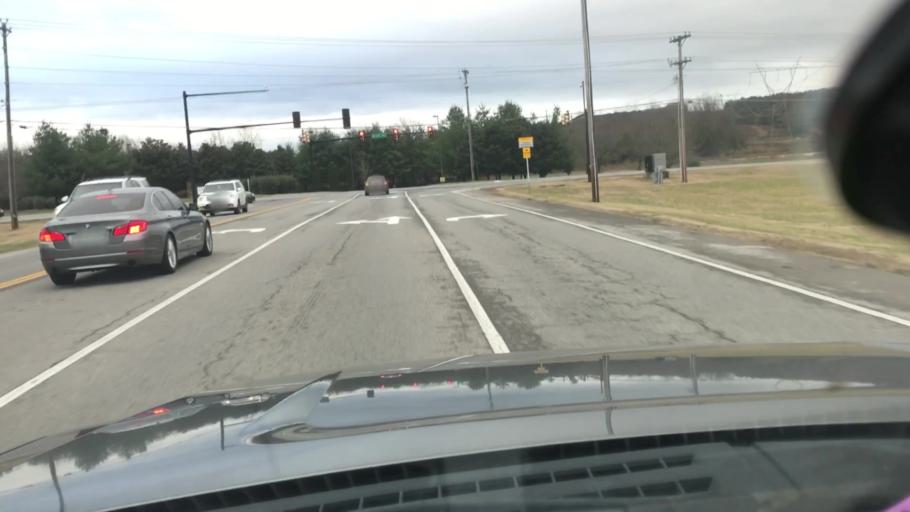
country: US
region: Tennessee
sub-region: Williamson County
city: Brentwood Estates
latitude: 35.9702
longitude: -86.7747
